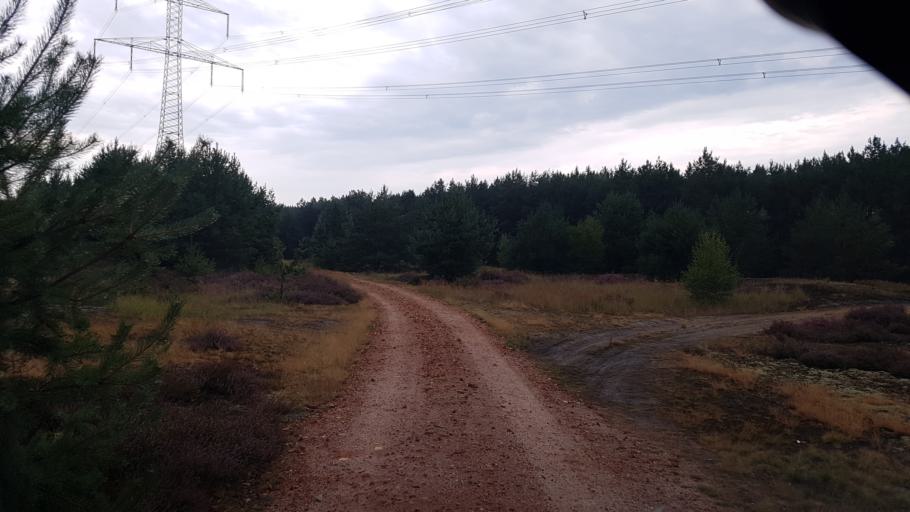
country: DE
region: Brandenburg
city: Sallgast
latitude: 51.6386
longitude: 13.7902
